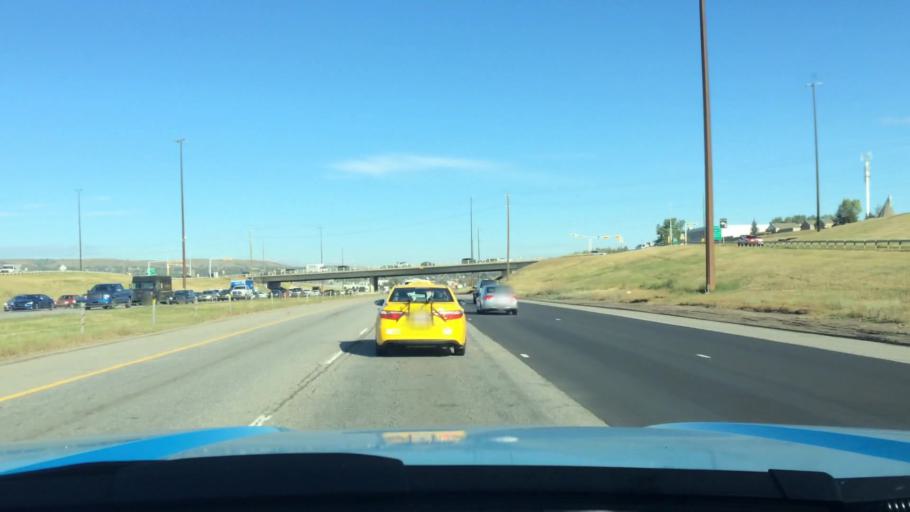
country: CA
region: Alberta
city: Calgary
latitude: 51.0796
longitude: -114.0314
